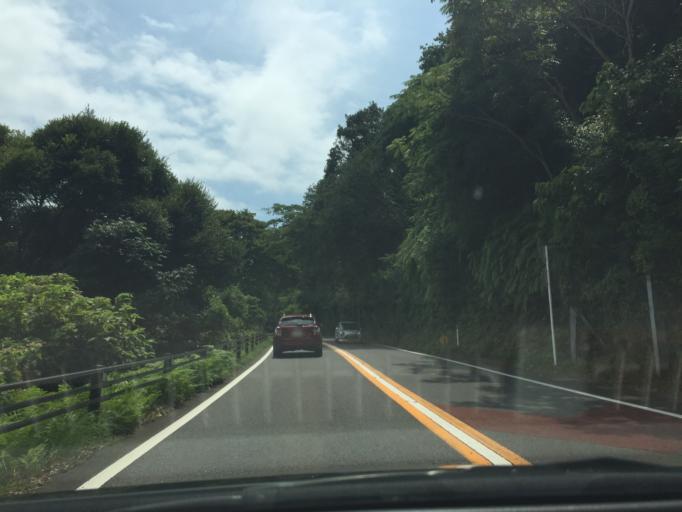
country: JP
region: Shizuoka
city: Shimoda
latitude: 34.7202
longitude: 138.9897
